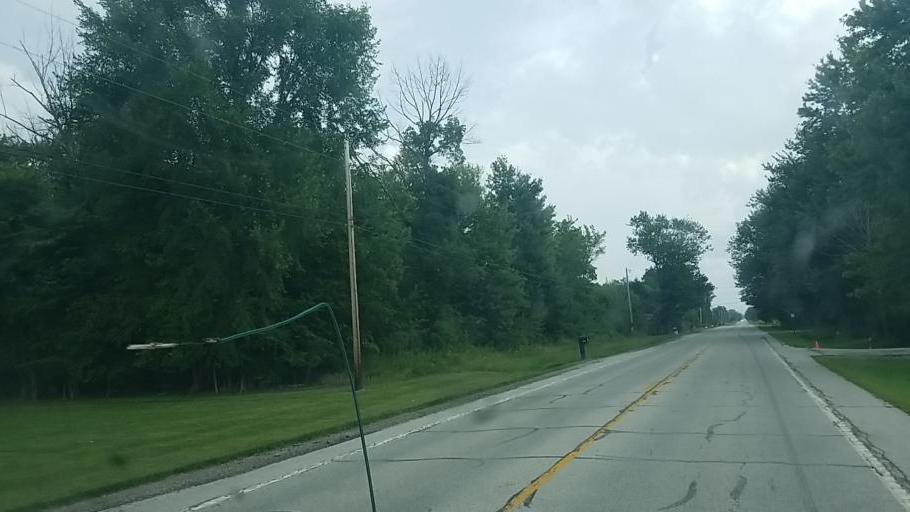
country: US
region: Ohio
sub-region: Lorain County
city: Lagrange
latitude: 41.1680
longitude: -82.0554
